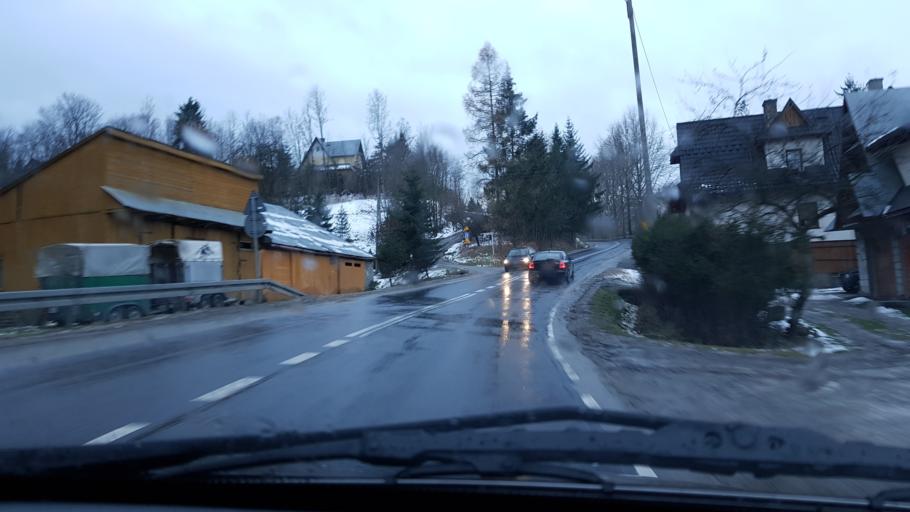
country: PL
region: Lesser Poland Voivodeship
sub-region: Powiat tatrzanski
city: Bukowina Tatrzanska
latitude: 49.3525
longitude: 20.1234
